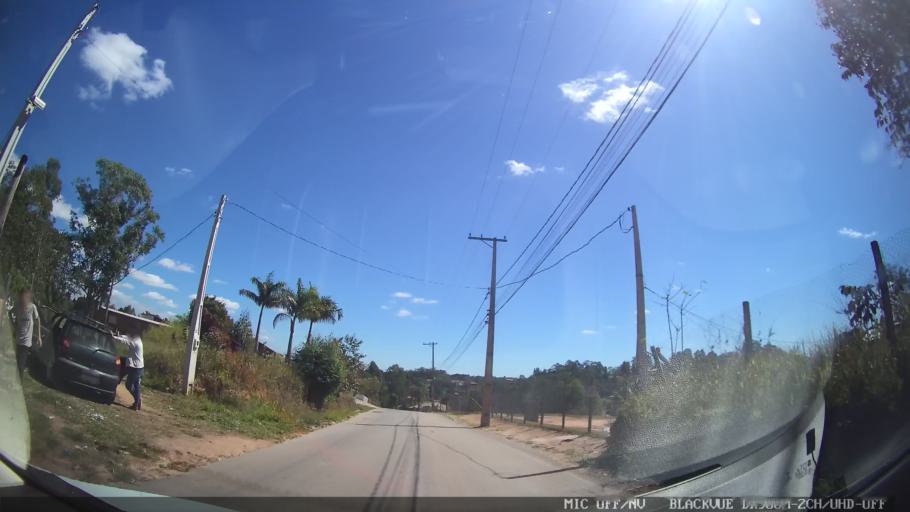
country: BR
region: Sao Paulo
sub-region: Campo Limpo Paulista
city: Campo Limpo Paulista
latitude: -23.1797
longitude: -46.7460
